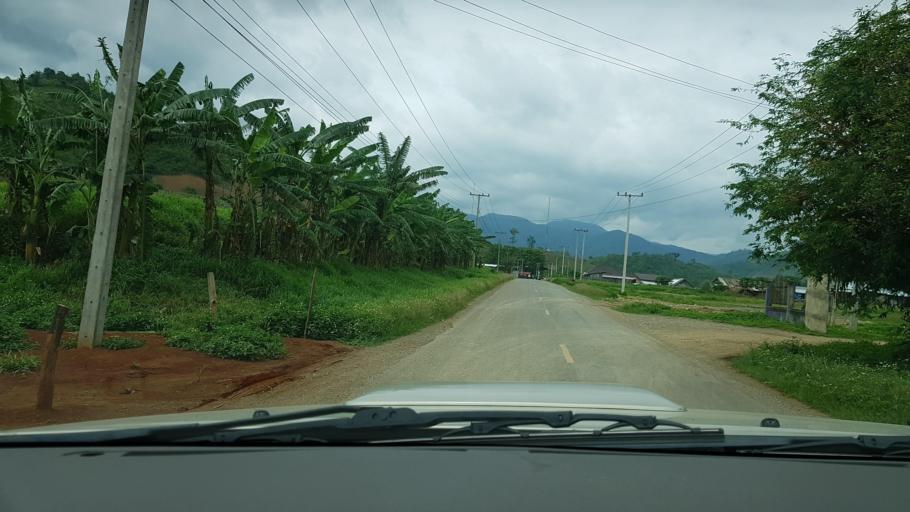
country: TH
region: Nan
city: Chaloem Phra Kiat
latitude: 19.9795
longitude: 101.2728
